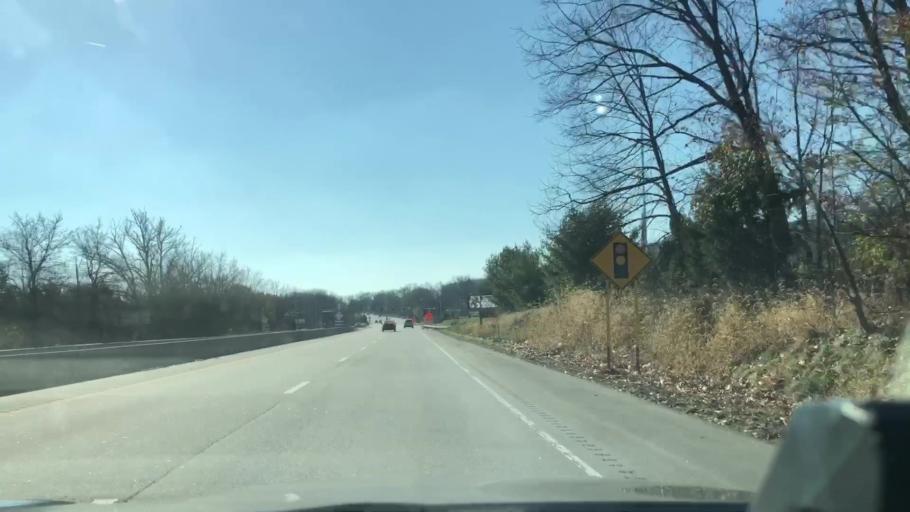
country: US
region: Pennsylvania
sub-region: Montgomery County
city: Halfway House
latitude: 40.2803
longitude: -75.6452
